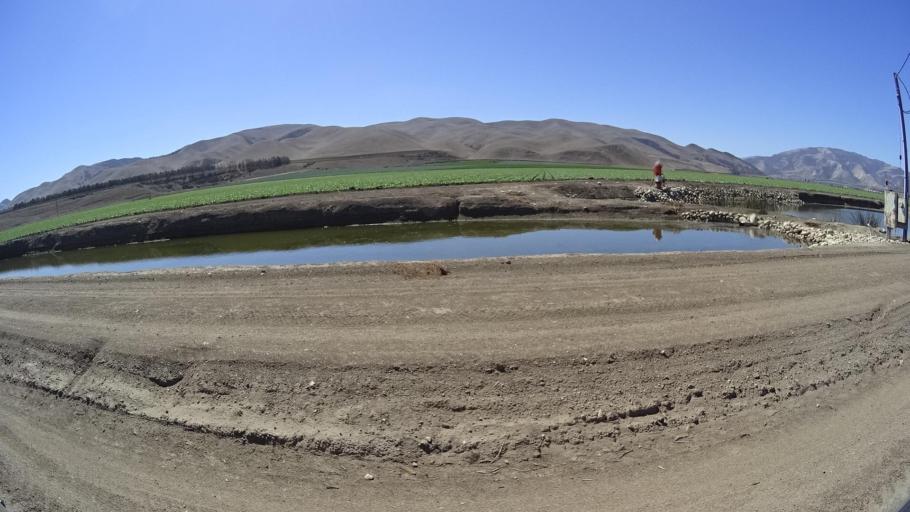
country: US
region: California
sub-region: Monterey County
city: Greenfield
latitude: 36.2871
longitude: -121.2400
